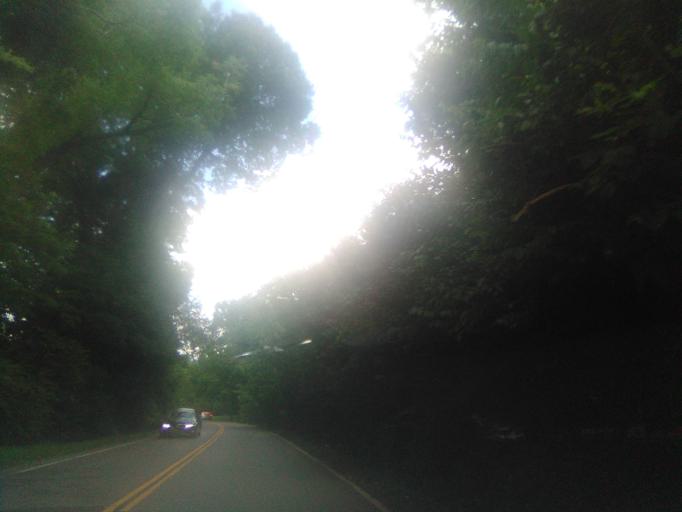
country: US
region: Tennessee
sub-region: Davidson County
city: Belle Meade
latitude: 36.1105
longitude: -86.8446
